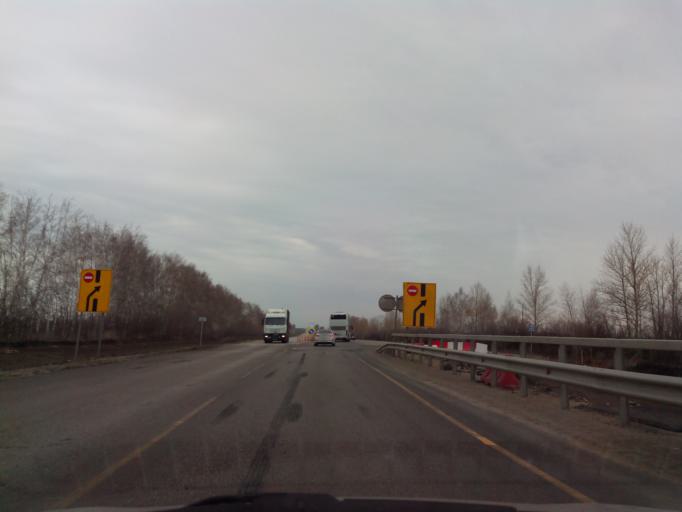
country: RU
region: Tambov
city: Selezni
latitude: 52.8071
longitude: 40.9653
